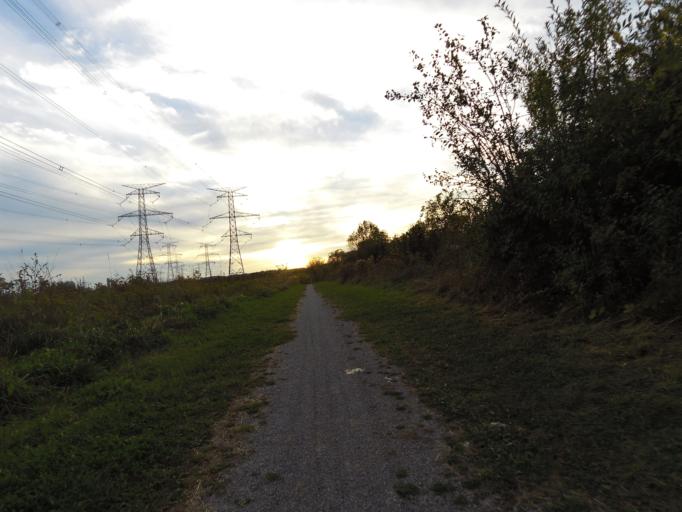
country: CA
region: Ontario
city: Oshawa
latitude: 43.8954
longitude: -78.6806
